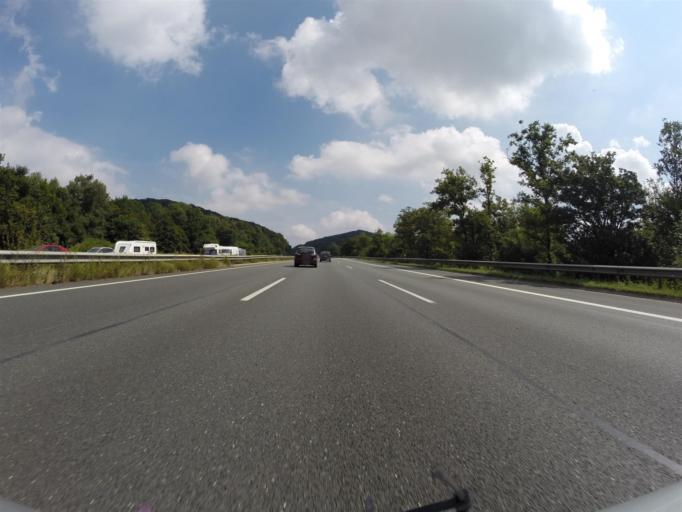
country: DE
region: North Rhine-Westphalia
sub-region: Regierungsbezirk Detmold
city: Oerlinghausen
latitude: 51.9653
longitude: 8.5972
